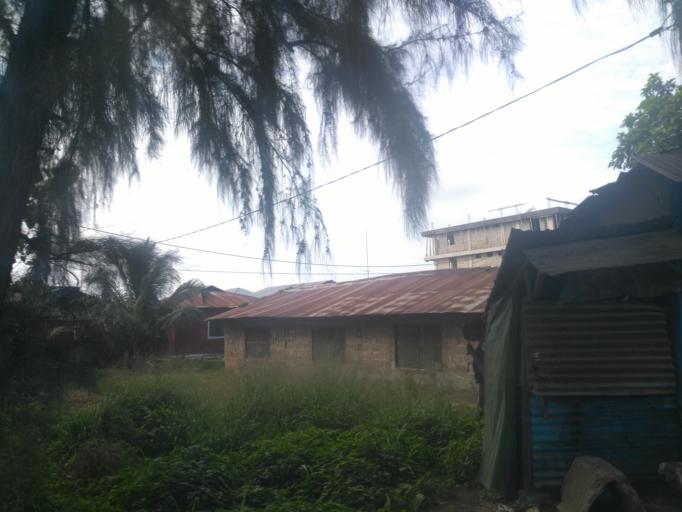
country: TZ
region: Zanzibar Urban/West
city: Zanzibar
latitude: -6.1588
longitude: 39.2064
